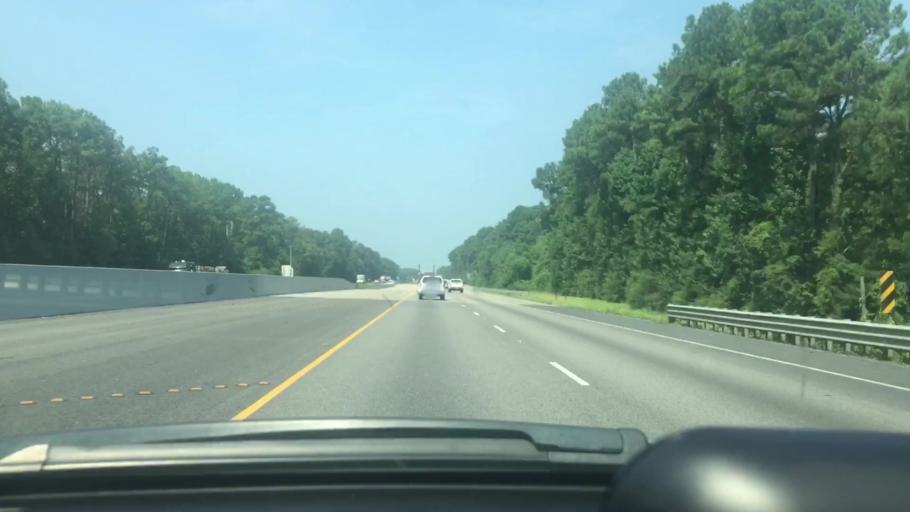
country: US
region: Louisiana
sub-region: Livingston Parish
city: Albany
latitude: 30.4748
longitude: -90.6515
